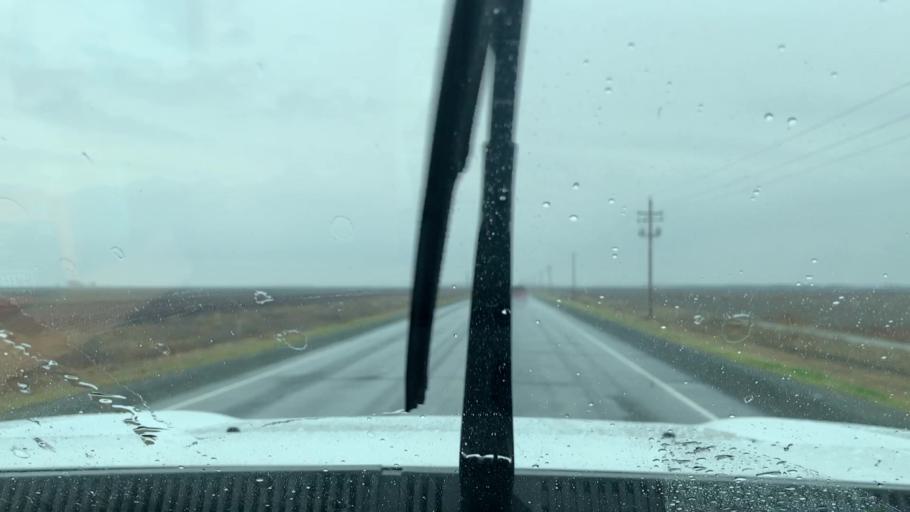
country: US
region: California
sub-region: Tulare County
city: Alpaugh
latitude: 35.9271
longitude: -119.4314
